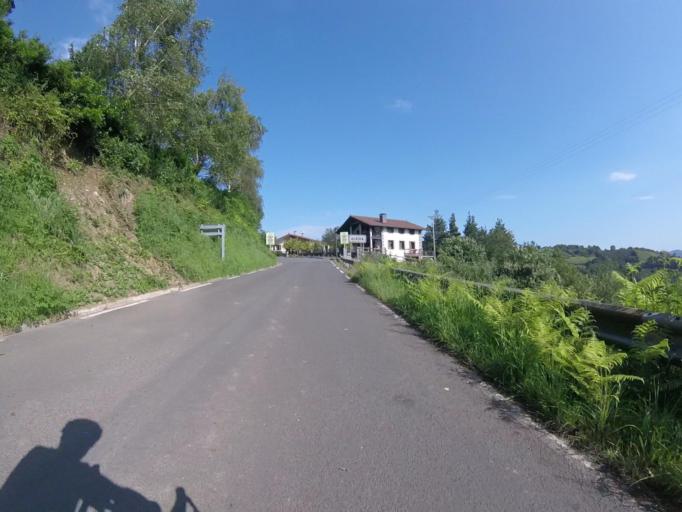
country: ES
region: Basque Country
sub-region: Provincia de Guipuzcoa
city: Alquiza
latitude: 43.1734
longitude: -2.1059
